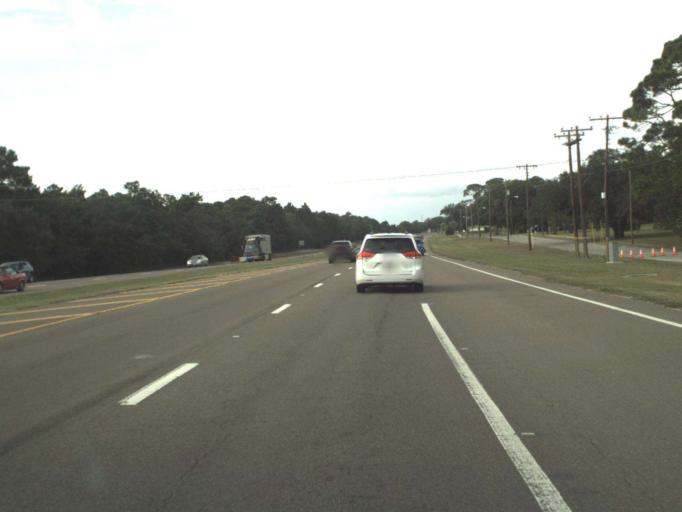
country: US
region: Florida
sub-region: Bay County
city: Tyndall Air Force Base
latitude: 30.0888
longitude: -85.6102
